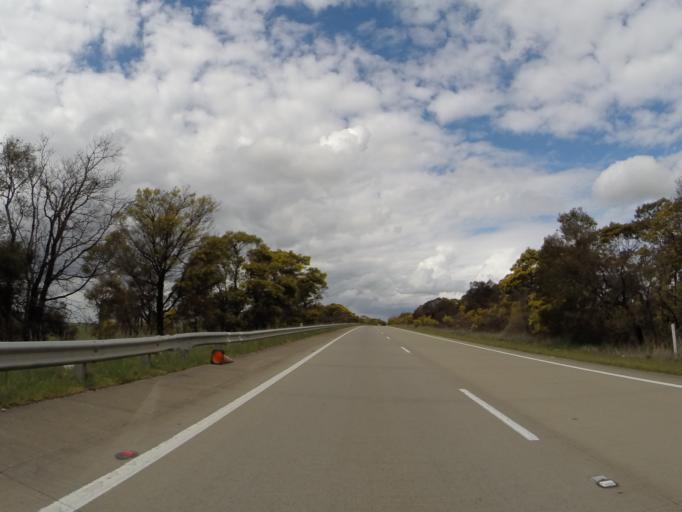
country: AU
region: New South Wales
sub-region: Goulburn Mulwaree
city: Goulburn
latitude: -34.8157
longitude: 149.4407
